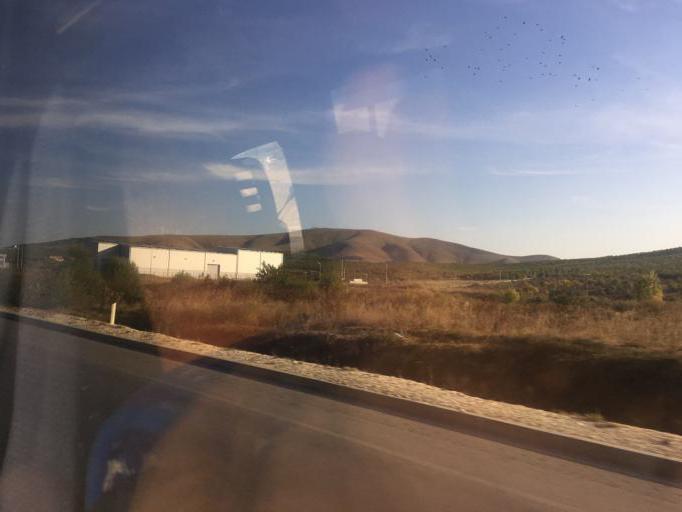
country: XK
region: Pristina
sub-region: Komuna e Drenasit
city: Glogovac
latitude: 42.6009
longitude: 20.9605
